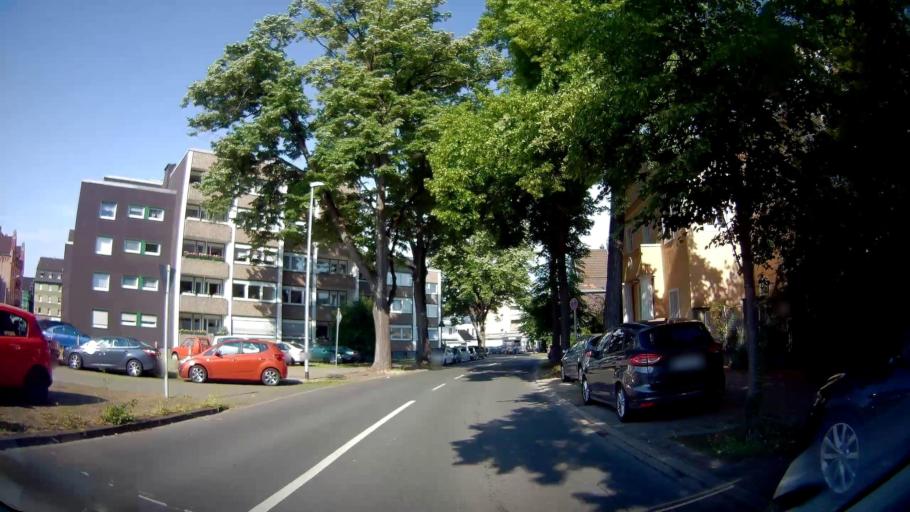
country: DE
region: North Rhine-Westphalia
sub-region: Regierungsbezirk Arnsberg
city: Herne
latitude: 51.5469
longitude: 7.2188
